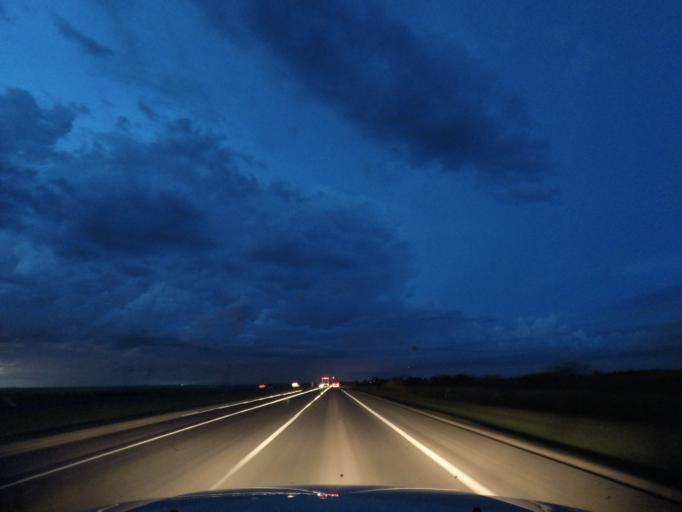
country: BR
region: Minas Gerais
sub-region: Uberlandia
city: Uberlandia
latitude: -19.2468
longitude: -48.1368
